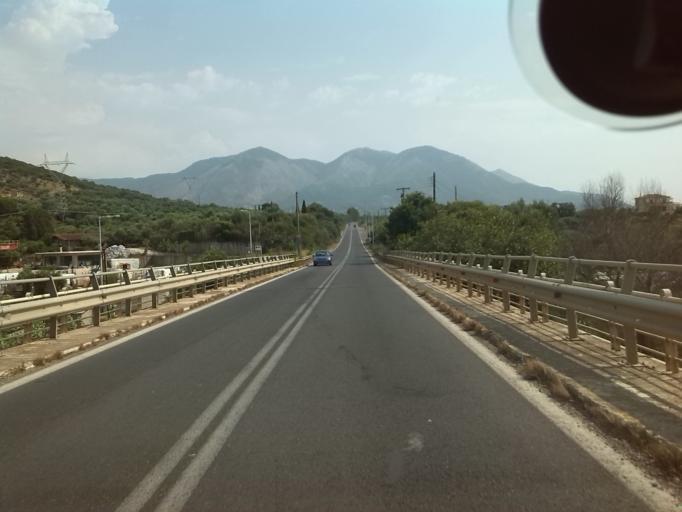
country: GR
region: Peloponnese
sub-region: Nomos Messinias
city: Kyparissia
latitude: 37.2928
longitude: 21.7024
